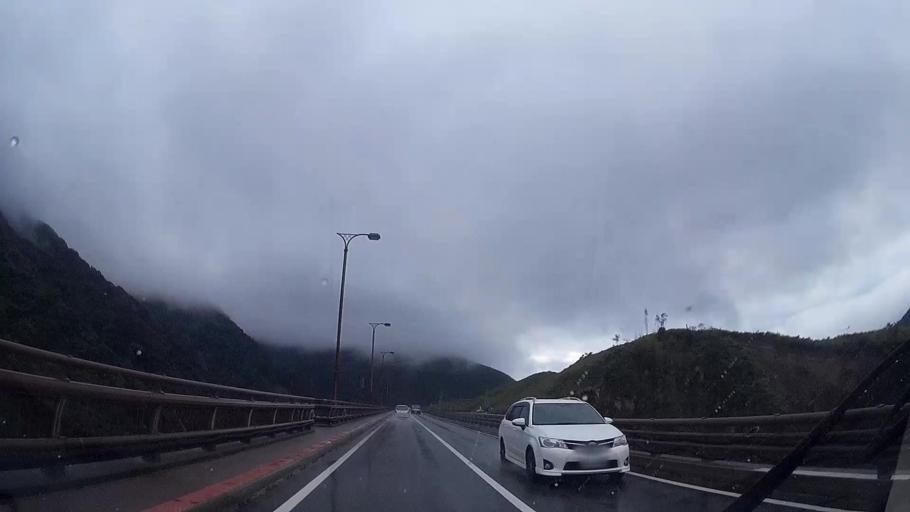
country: JP
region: Kumamoto
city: Aso
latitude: 32.8751
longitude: 130.9849
